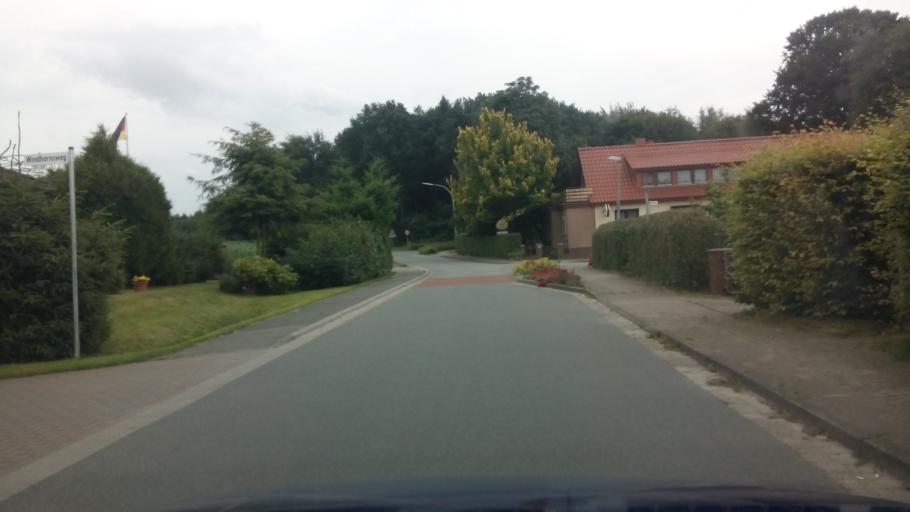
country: DE
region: Lower Saxony
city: Hambergen
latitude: 53.3049
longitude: 8.8266
